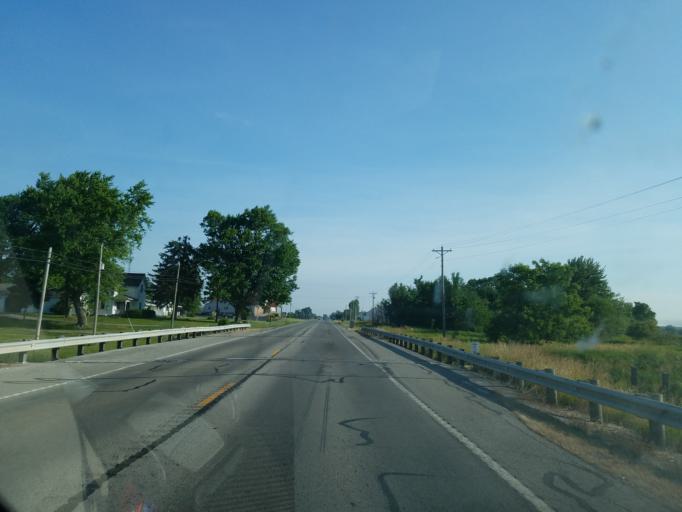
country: US
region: Ohio
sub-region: Hardin County
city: Kenton
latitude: 40.7162
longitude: -83.6234
